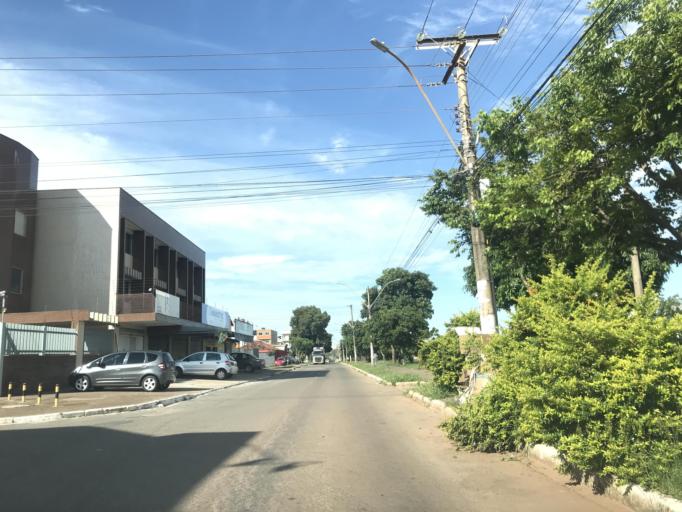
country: BR
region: Federal District
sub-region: Brasilia
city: Brasilia
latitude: -15.8532
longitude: -48.0407
